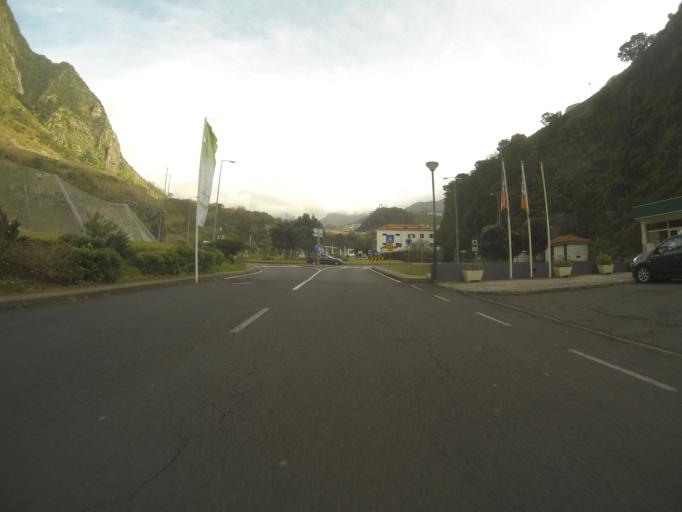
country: PT
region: Madeira
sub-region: Sao Vicente
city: Sao Vicente
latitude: 32.8059
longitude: -17.0467
